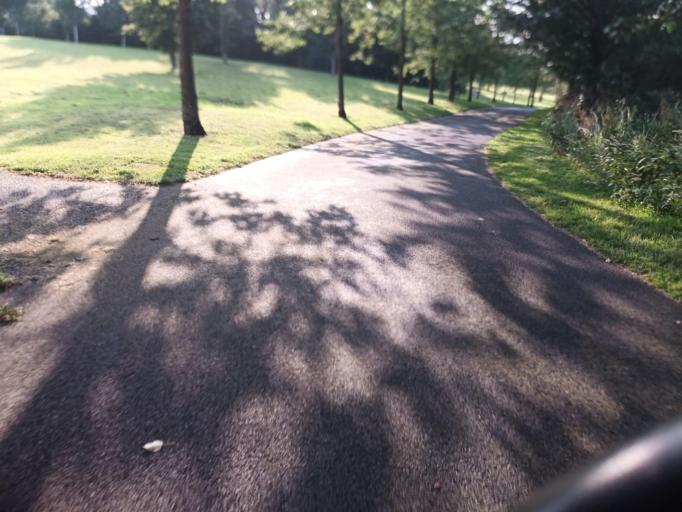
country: GB
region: Northern Ireland
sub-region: Castlereagh District
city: Dundonald
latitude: 54.5849
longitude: -5.7918
